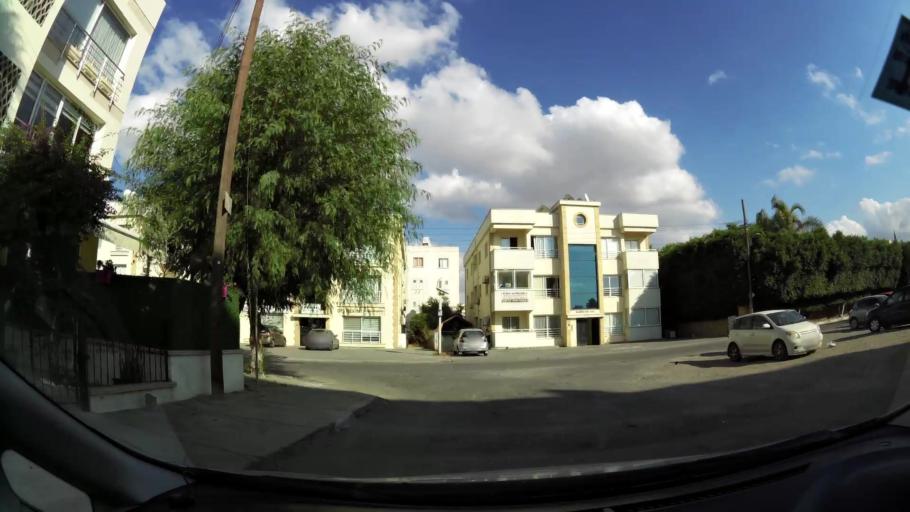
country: CY
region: Lefkosia
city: Nicosia
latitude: 35.1956
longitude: 33.3605
